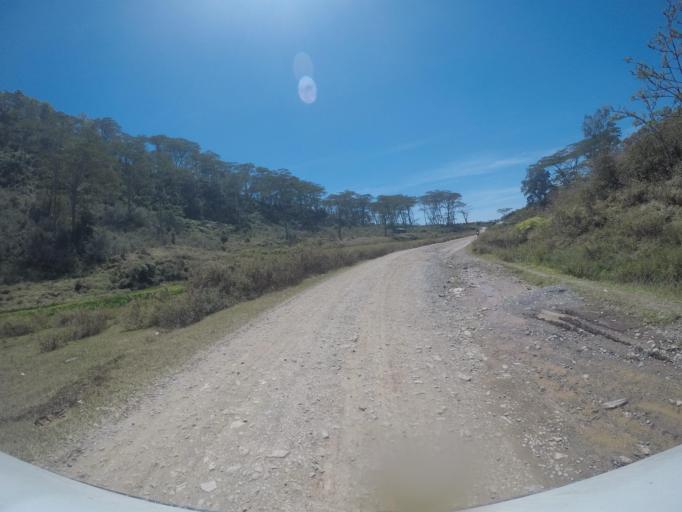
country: TL
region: Ermera
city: Gleno
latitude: -8.7745
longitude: 125.3936
